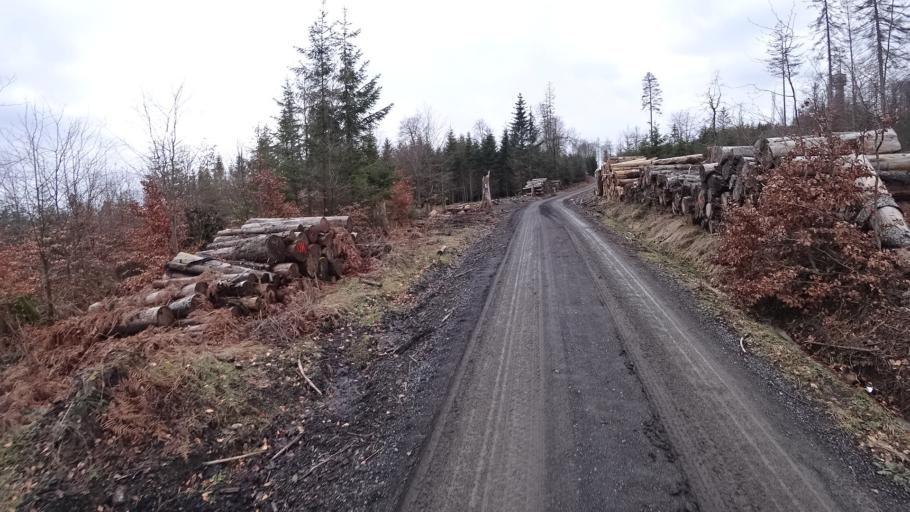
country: DE
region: Rheinland-Pfalz
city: Ebernhahn
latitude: 50.4294
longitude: 7.7567
